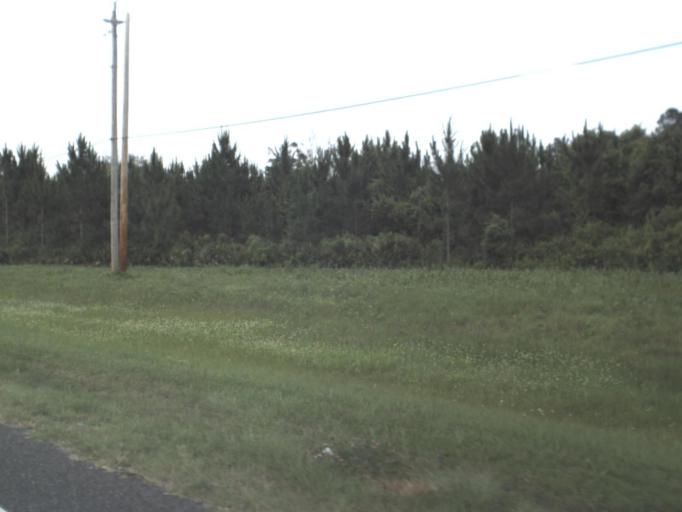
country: US
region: Florida
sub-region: Putnam County
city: Palatka
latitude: 29.6821
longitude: -81.6613
